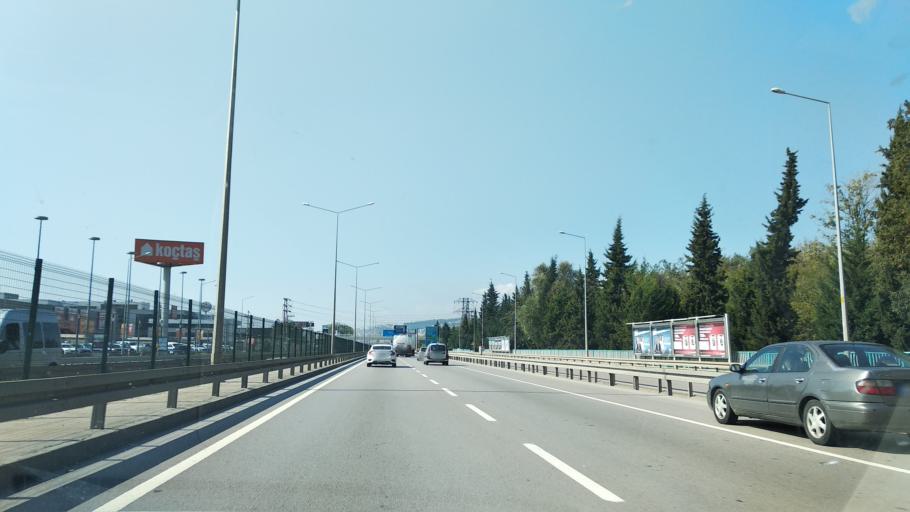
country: TR
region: Kocaeli
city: Kullar
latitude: 40.7598
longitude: 29.9791
